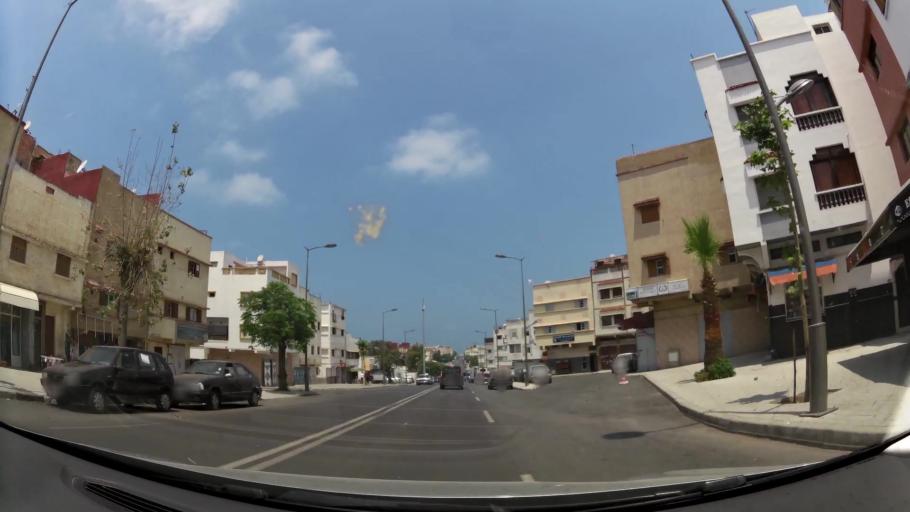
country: MA
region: Rabat-Sale-Zemmour-Zaer
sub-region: Rabat
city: Rabat
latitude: 33.9835
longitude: -6.8769
